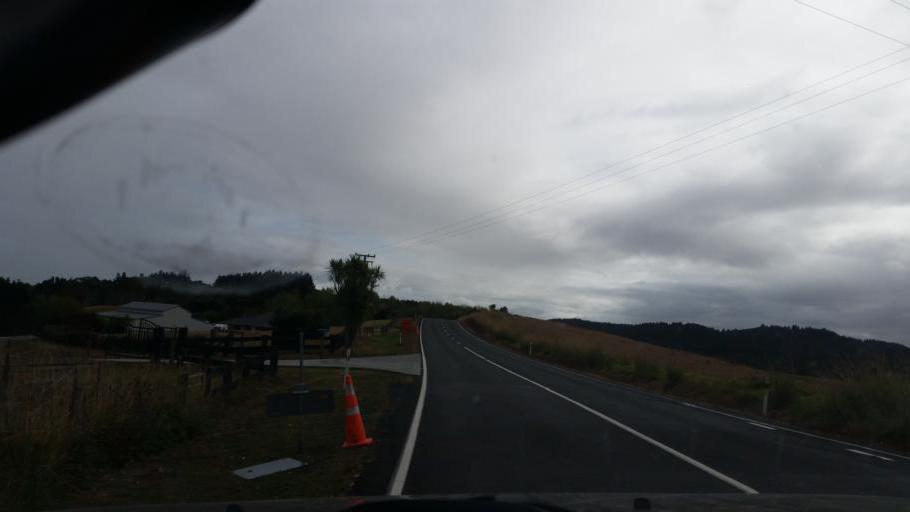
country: NZ
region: Auckland
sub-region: Auckland
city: Wellsford
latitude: -36.2179
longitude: 174.3886
